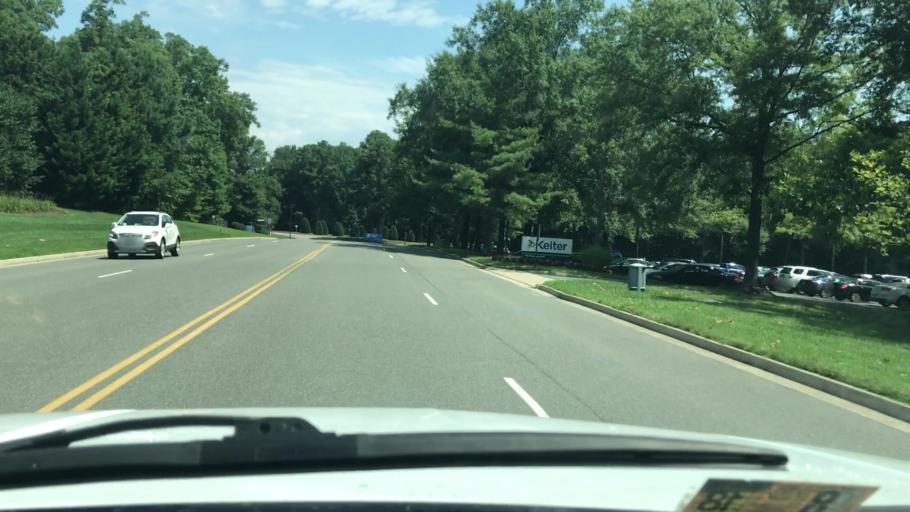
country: US
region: Virginia
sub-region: Henrico County
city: Short Pump
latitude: 37.6530
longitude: -77.5849
